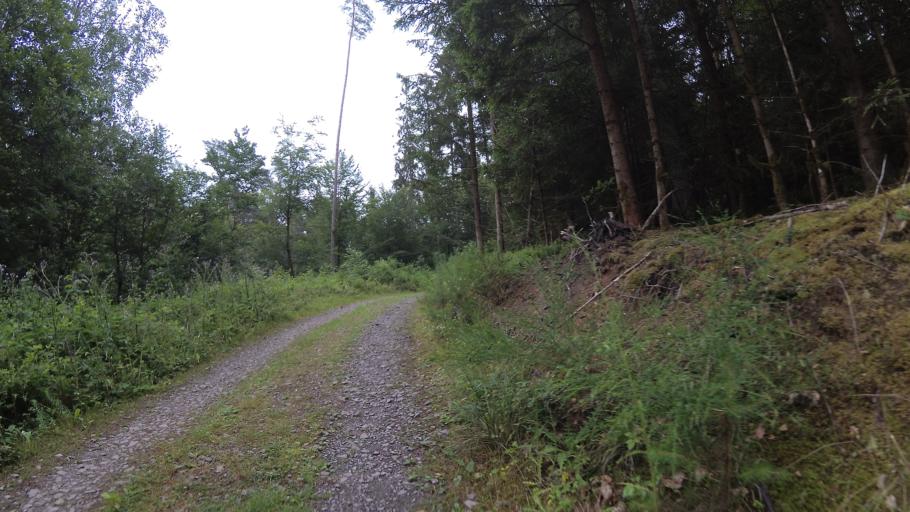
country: DE
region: Rheinland-Pfalz
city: Bechhofen
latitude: 49.3173
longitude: 7.3776
